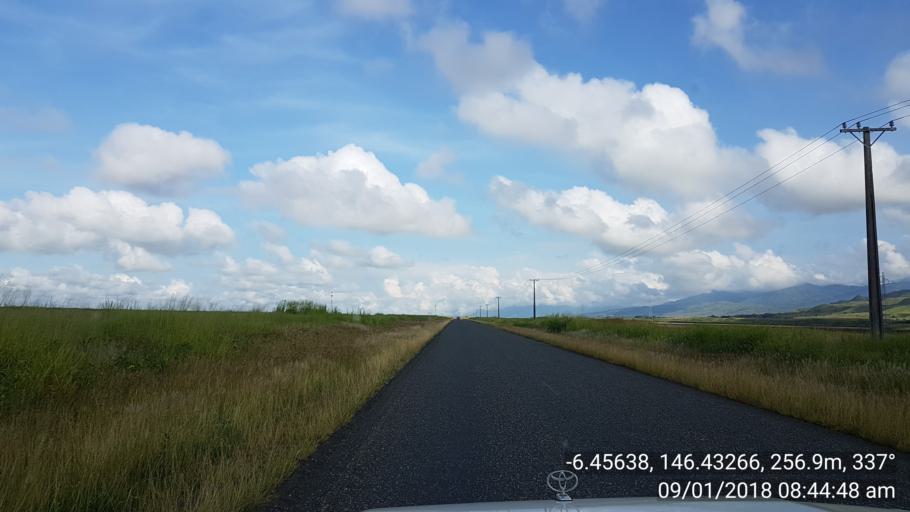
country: PG
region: Eastern Highlands
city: Kainantu
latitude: -6.4565
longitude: 146.4325
